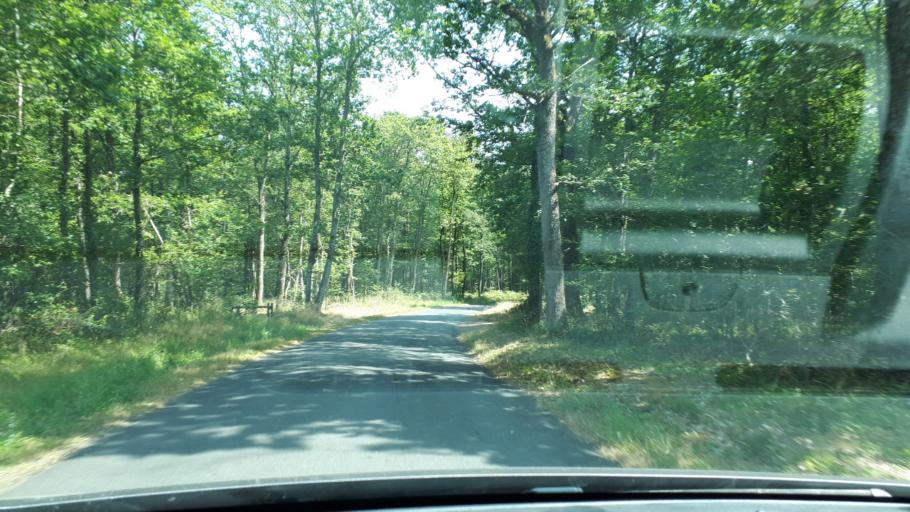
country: FR
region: Centre
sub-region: Departement du Loir-et-Cher
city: Naveil
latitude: 47.8298
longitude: 1.0386
